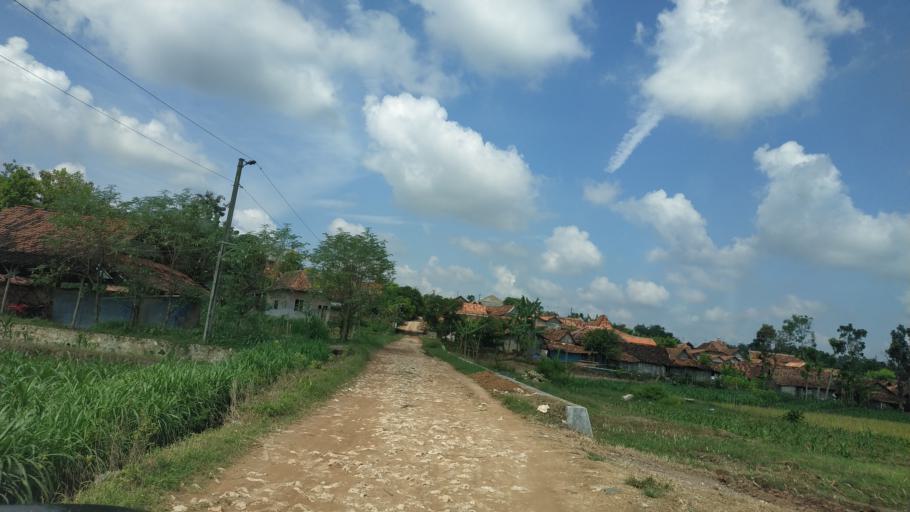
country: ID
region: Central Java
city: Guyangan
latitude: -7.0059
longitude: 111.1051
